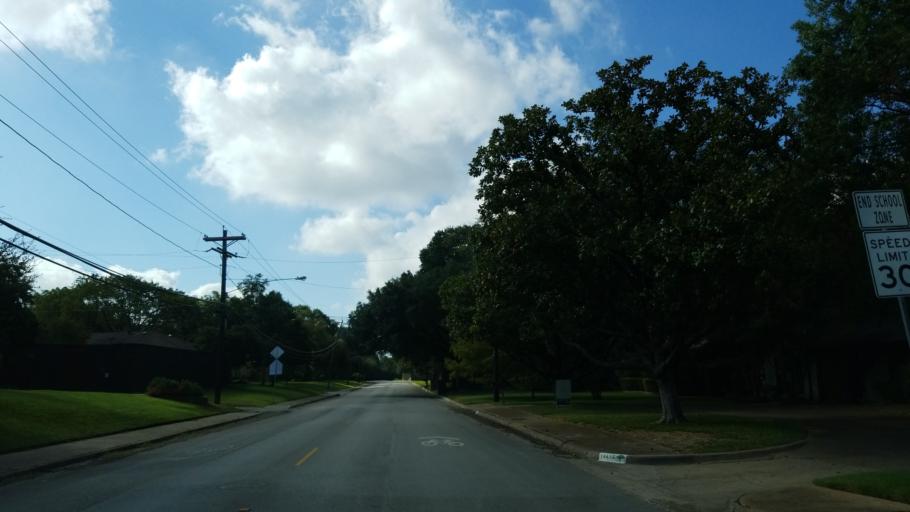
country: US
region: Texas
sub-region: Dallas County
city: Richardson
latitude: 32.9452
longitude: -96.7781
